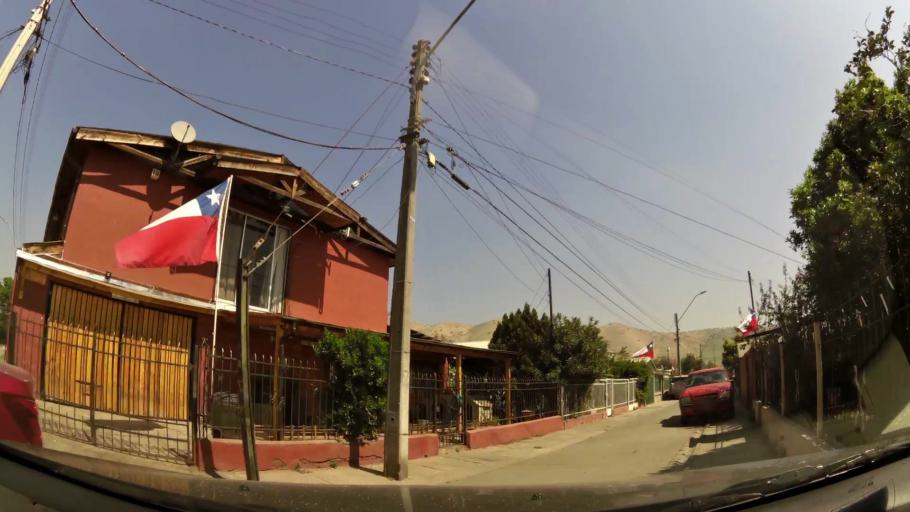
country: CL
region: Santiago Metropolitan
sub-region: Provincia de Maipo
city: San Bernardo
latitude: -33.5836
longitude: -70.7126
